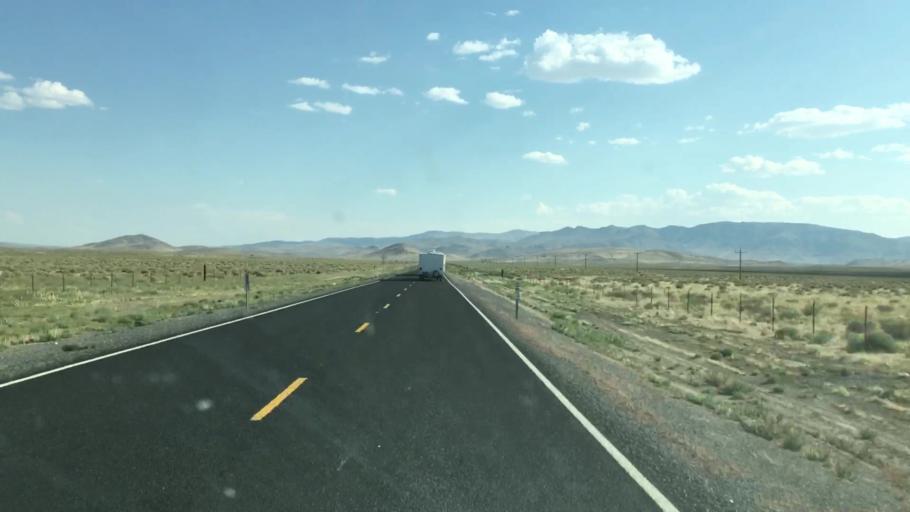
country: US
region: Nevada
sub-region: Lyon County
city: Fernley
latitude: 39.6709
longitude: -119.3323
